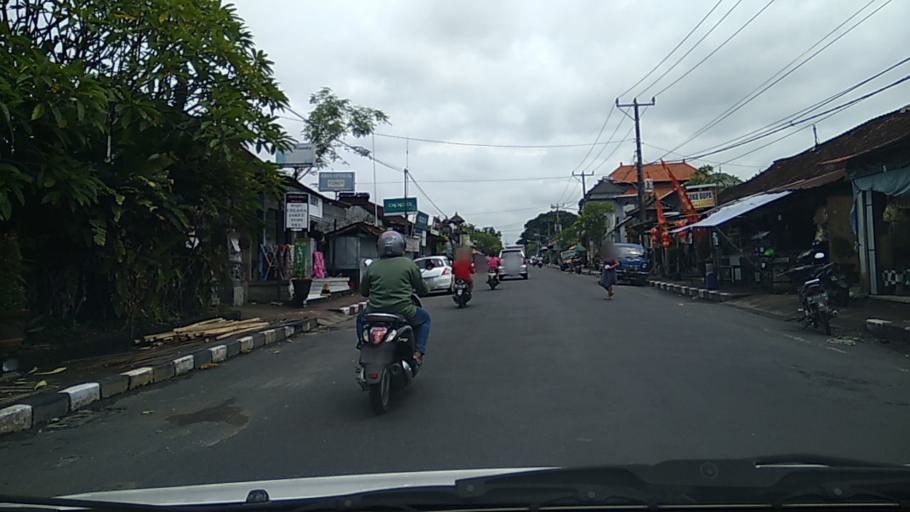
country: ID
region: Bali
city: Banjar Kembangsari
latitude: -8.5153
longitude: 115.2099
